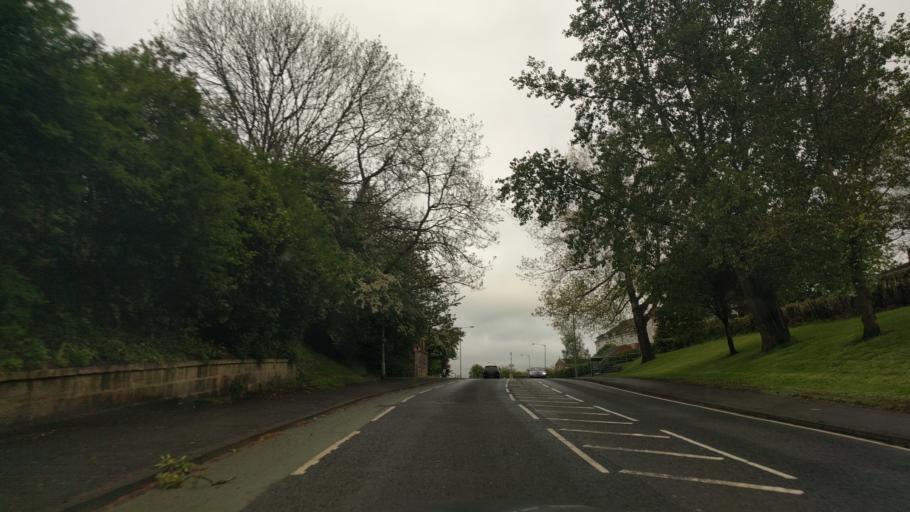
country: GB
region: England
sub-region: Northumberland
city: Morpeth
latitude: 55.1611
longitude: -1.6826
